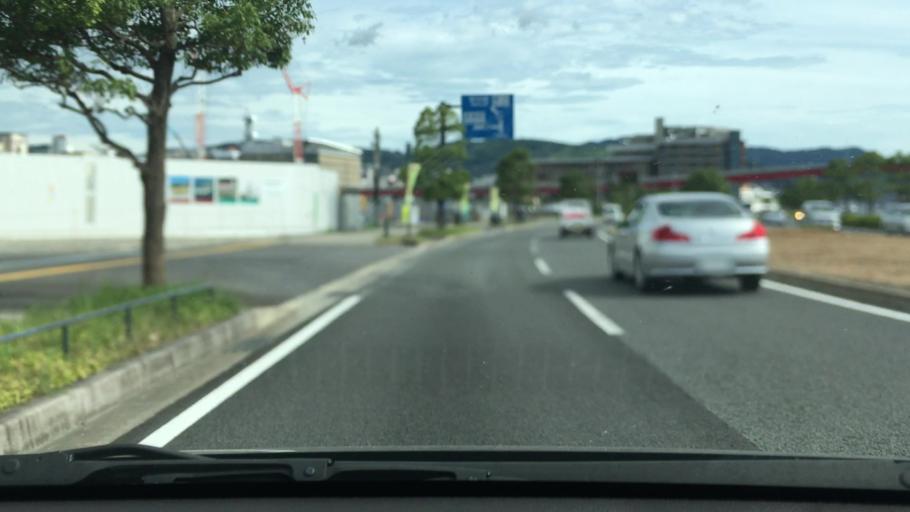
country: JP
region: Nagasaki
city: Nagasaki-shi
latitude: 32.7545
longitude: 129.8670
